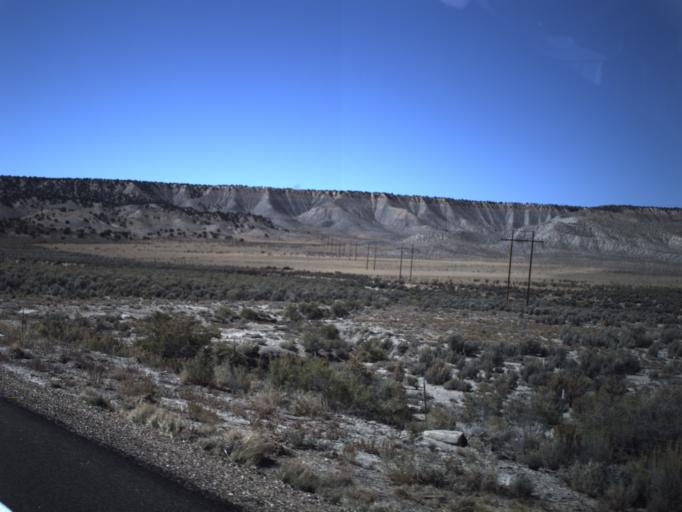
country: US
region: Utah
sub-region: Garfield County
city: Panguitch
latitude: 37.6029
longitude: -111.9648
